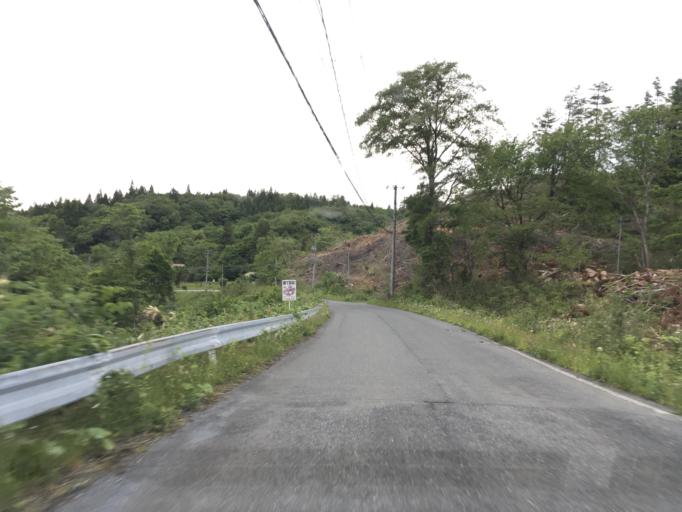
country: JP
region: Iwate
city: Mizusawa
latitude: 39.1673
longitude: 141.3025
